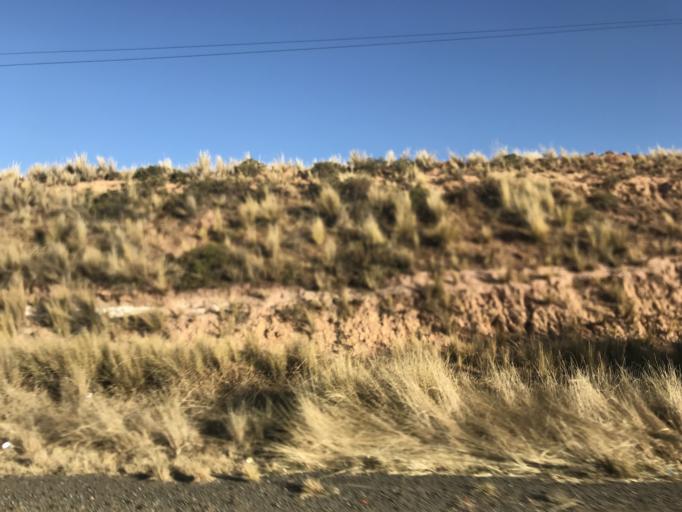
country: BO
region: La Paz
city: Tiahuanaco
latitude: -16.5639
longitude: -68.6320
